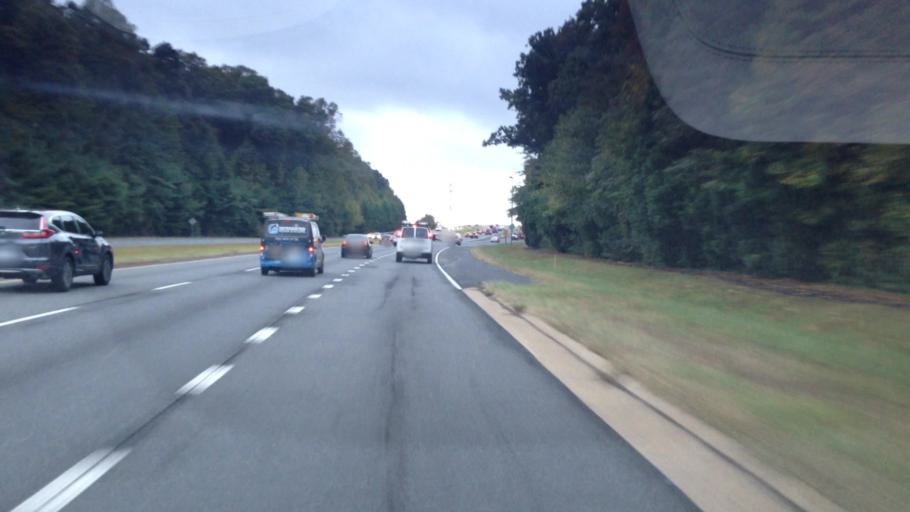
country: US
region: Virginia
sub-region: Fairfax County
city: Greenbriar
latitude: 38.8395
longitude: -77.3740
